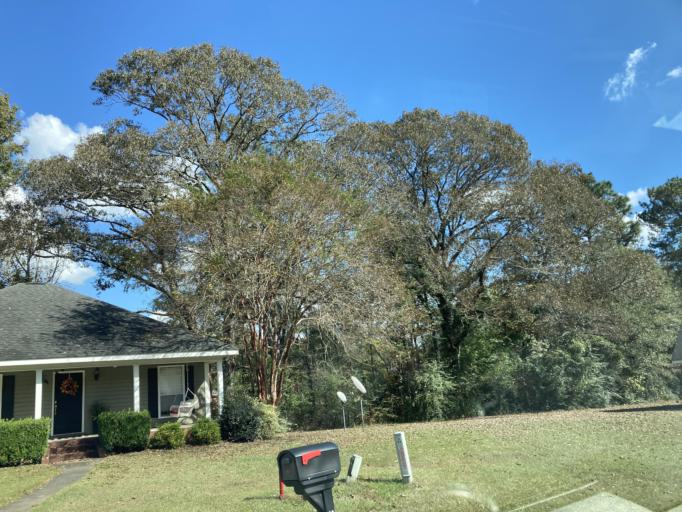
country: US
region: Mississippi
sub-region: Lamar County
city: West Hattiesburg
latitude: 31.2672
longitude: -89.3871
